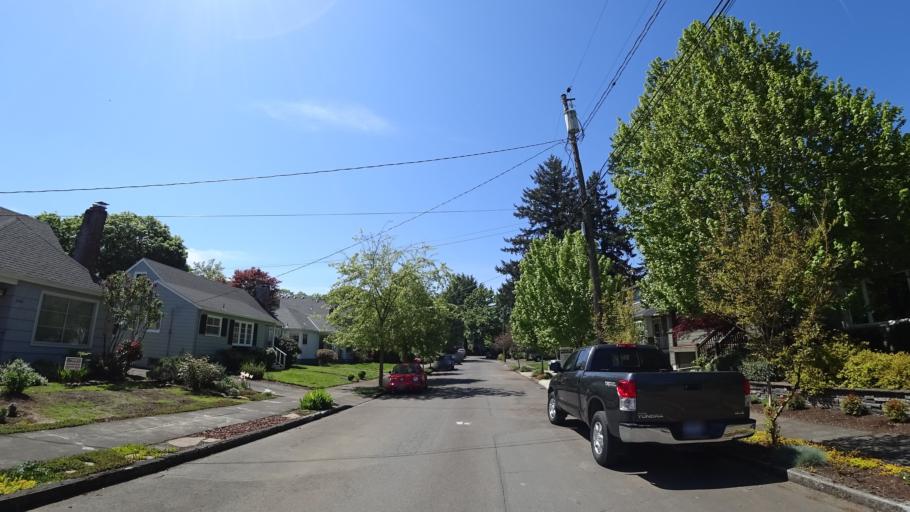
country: US
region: Oregon
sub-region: Clackamas County
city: Milwaukie
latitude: 45.4678
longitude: -122.6248
